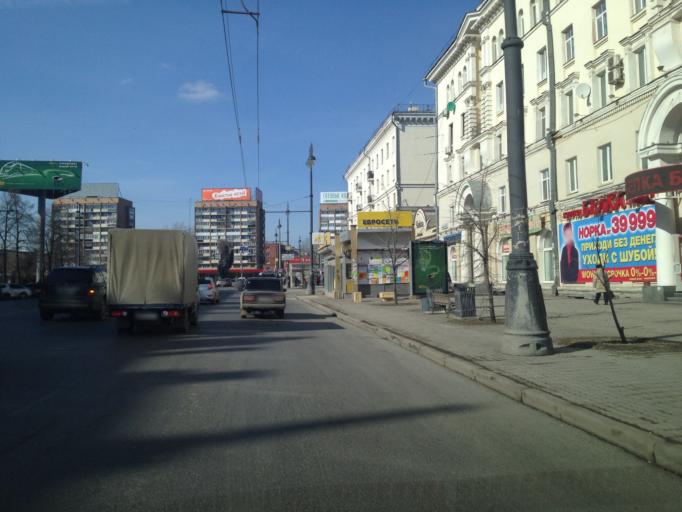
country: RU
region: Sverdlovsk
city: Yekaterinburg
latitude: 56.8545
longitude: 60.6045
